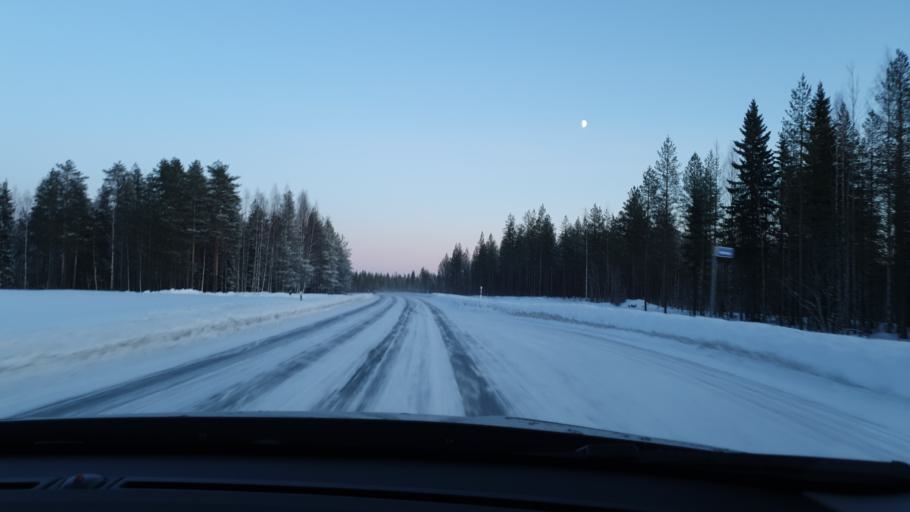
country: FI
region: Kainuu
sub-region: Kehys-Kainuu
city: Kuhmo
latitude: 64.0845
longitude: 29.0610
